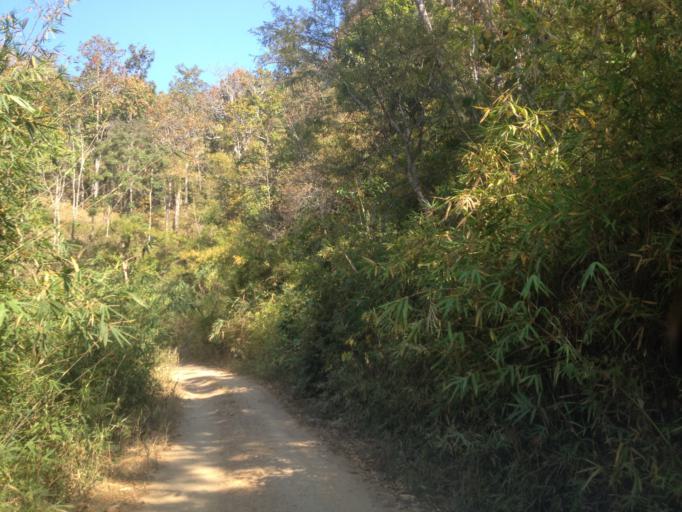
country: TH
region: Mae Hong Son
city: Ban Huai I Huak
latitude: 18.1317
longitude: 98.1934
